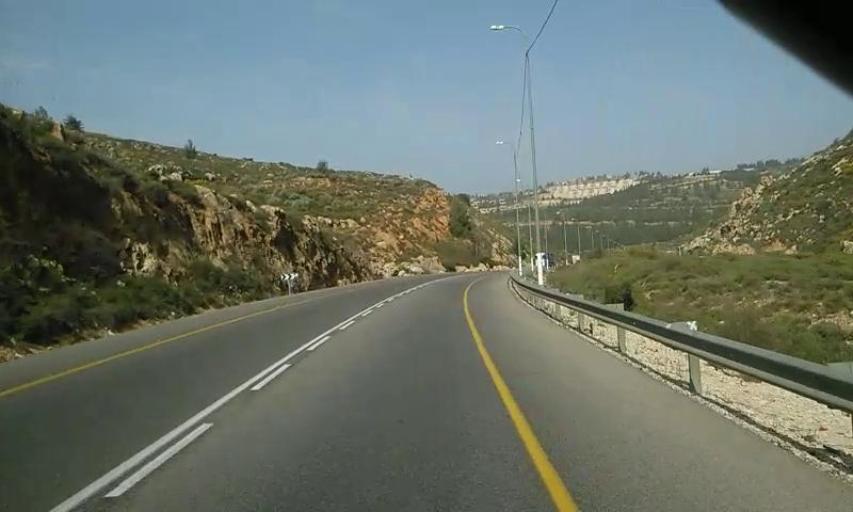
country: PS
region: West Bank
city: Qaryut
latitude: 32.0647
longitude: 35.2745
